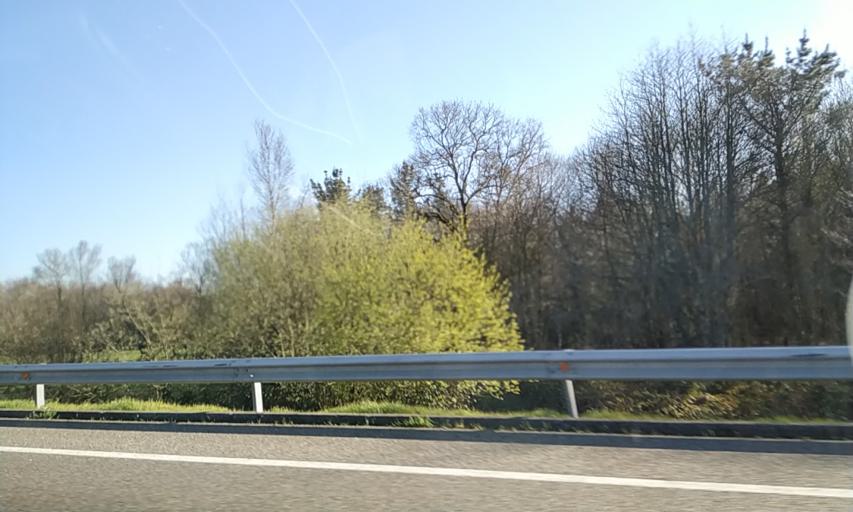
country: ES
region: Galicia
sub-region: Provincia de Lugo
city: Guitiriz
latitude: 43.1910
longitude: -7.8672
